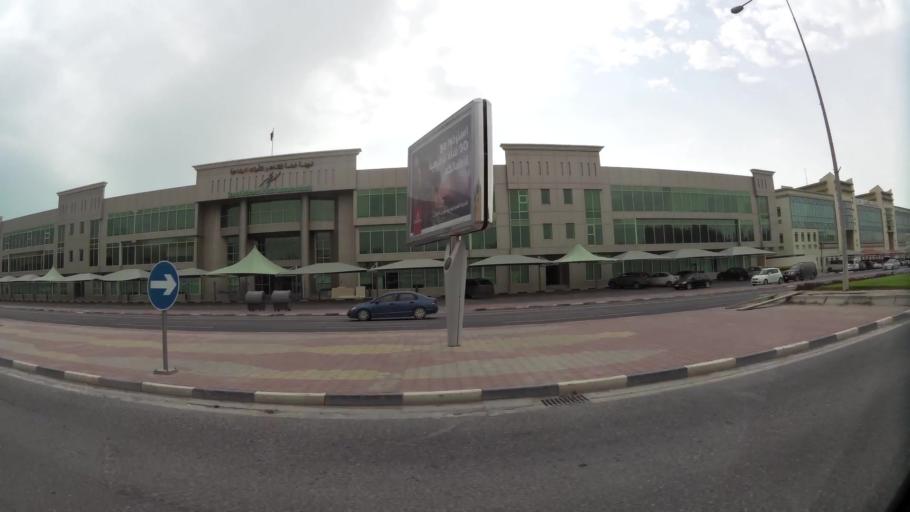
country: QA
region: Baladiyat ad Dawhah
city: Doha
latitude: 25.2971
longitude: 51.4985
